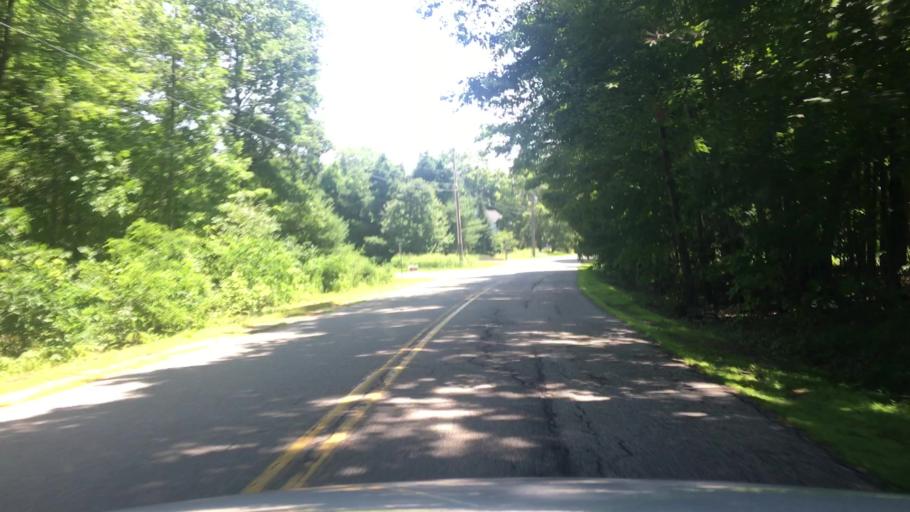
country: US
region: Maine
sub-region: Cumberland County
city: Cumberland Center
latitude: 43.7606
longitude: -70.2751
